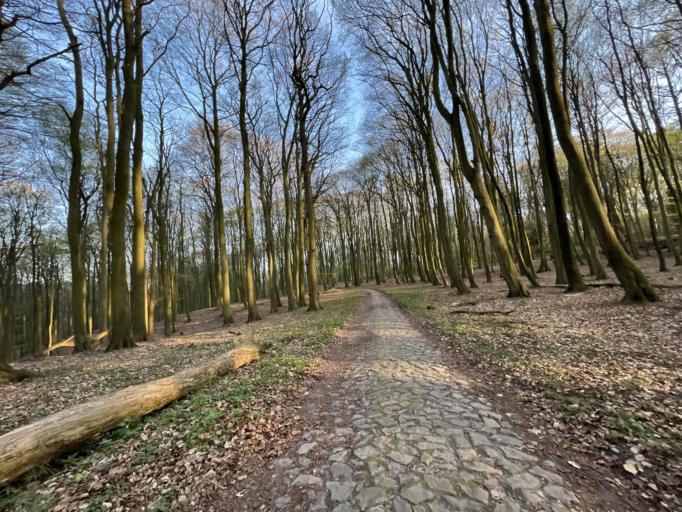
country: DE
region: Mecklenburg-Vorpommern
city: Sassnitz
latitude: 54.5319
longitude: 13.6527
